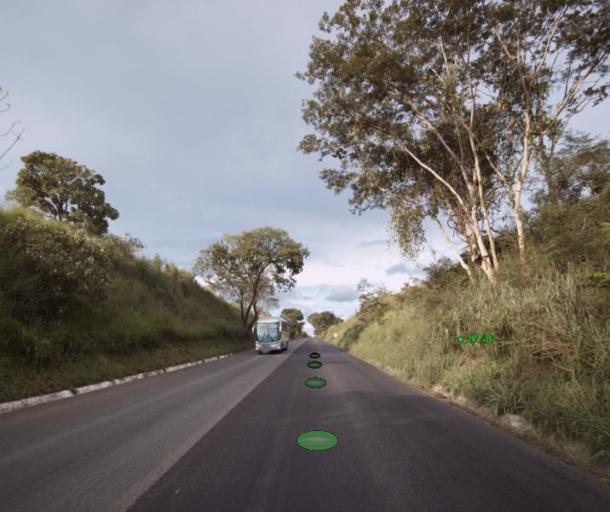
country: BR
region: Goias
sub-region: Itapaci
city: Itapaci
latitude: -15.1258
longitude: -49.5070
